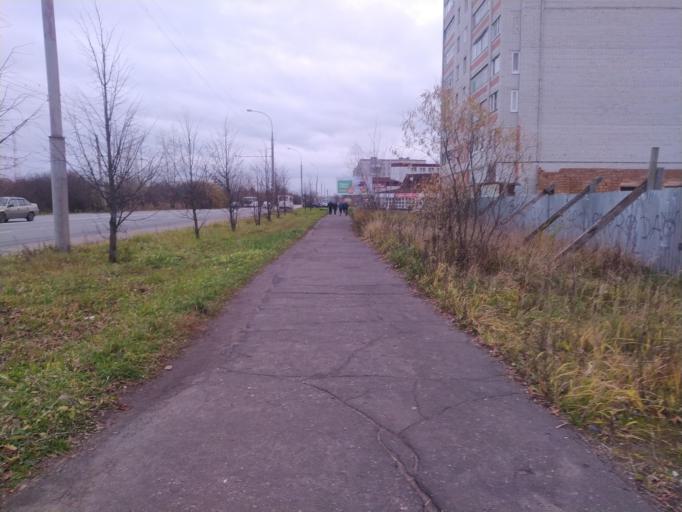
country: RU
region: Jaroslavl
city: Rybinsk
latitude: 58.0465
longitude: 38.7844
